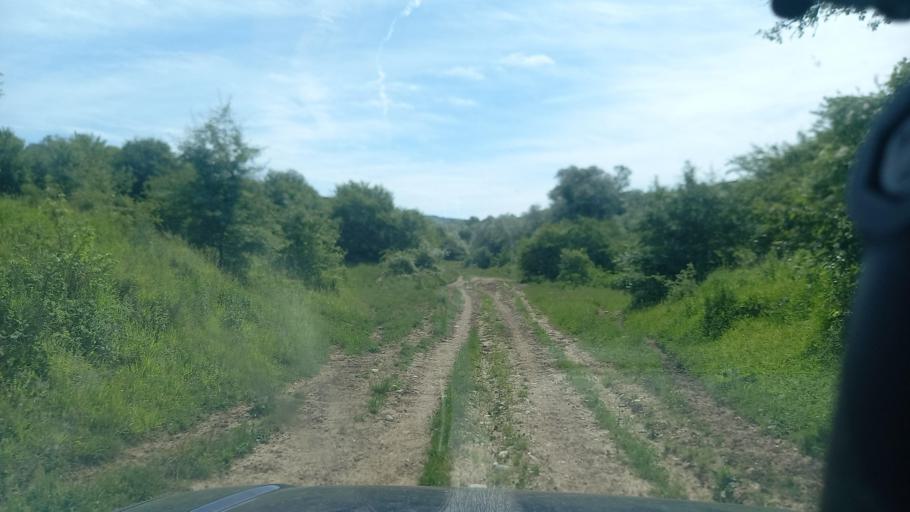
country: RU
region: Karachayevo-Cherkesiya
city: Kurdzhinovo
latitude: 44.1407
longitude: 41.0651
